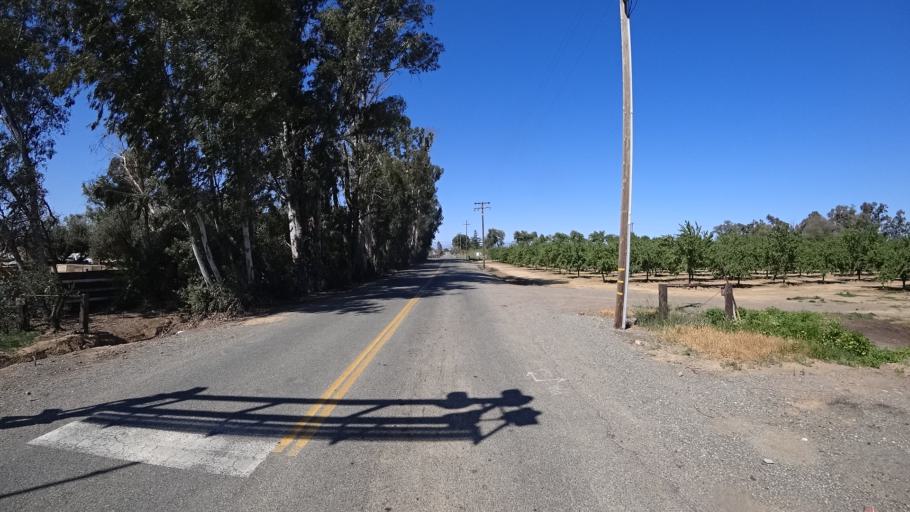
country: US
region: California
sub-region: Glenn County
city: Orland
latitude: 39.7112
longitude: -122.1955
